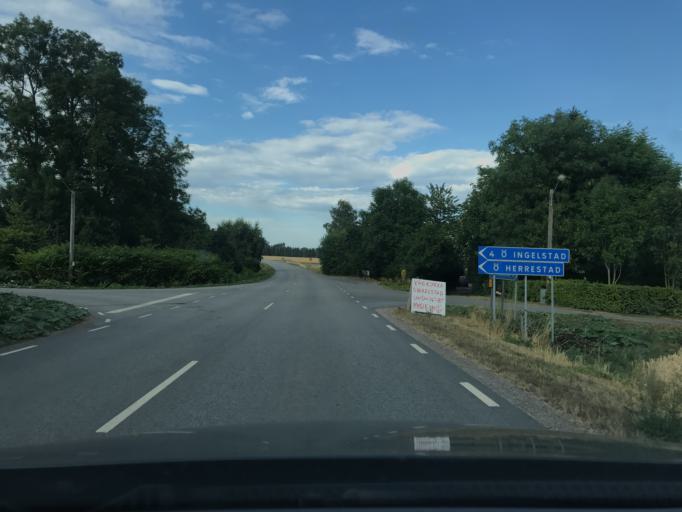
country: SE
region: Skane
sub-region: Simrishamns Kommun
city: Kivik
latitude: 55.5241
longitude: 14.1670
